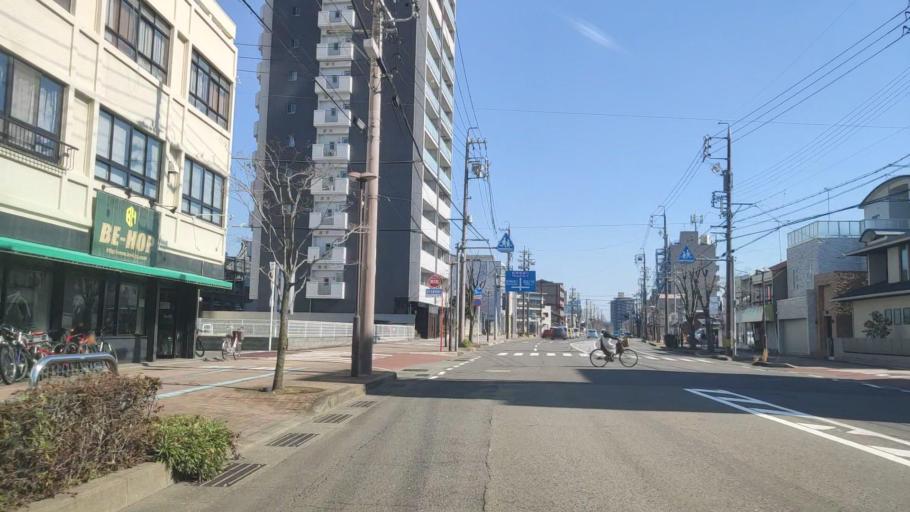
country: JP
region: Gifu
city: Gifu-shi
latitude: 35.4063
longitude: 136.7536
